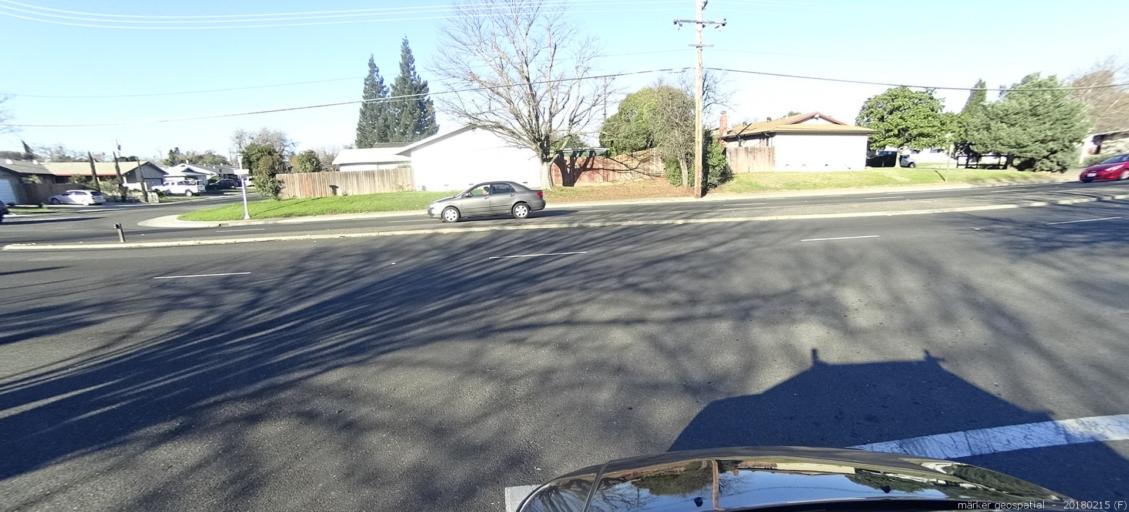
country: US
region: California
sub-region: Sacramento County
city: Foothill Farms
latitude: 38.6724
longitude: -121.3365
